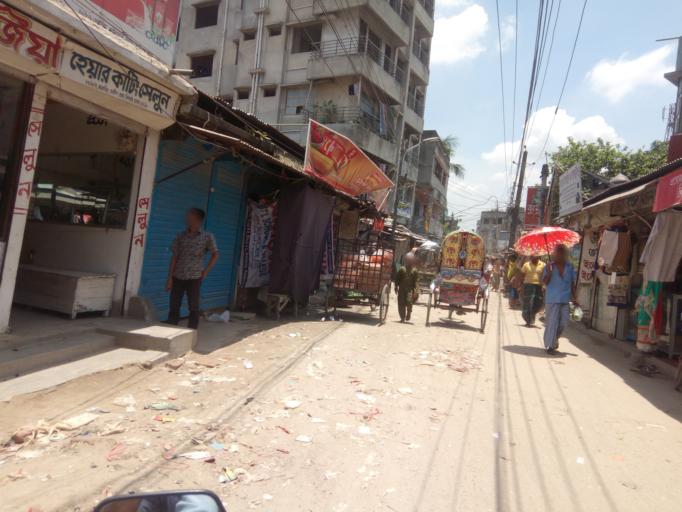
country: BD
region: Dhaka
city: Paltan
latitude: 23.7552
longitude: 90.4347
